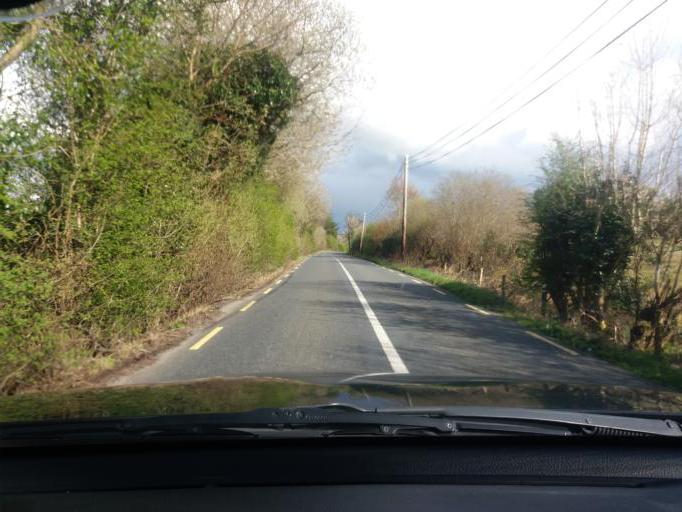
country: IE
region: Connaught
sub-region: County Leitrim
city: Manorhamilton
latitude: 54.3421
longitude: -8.2289
